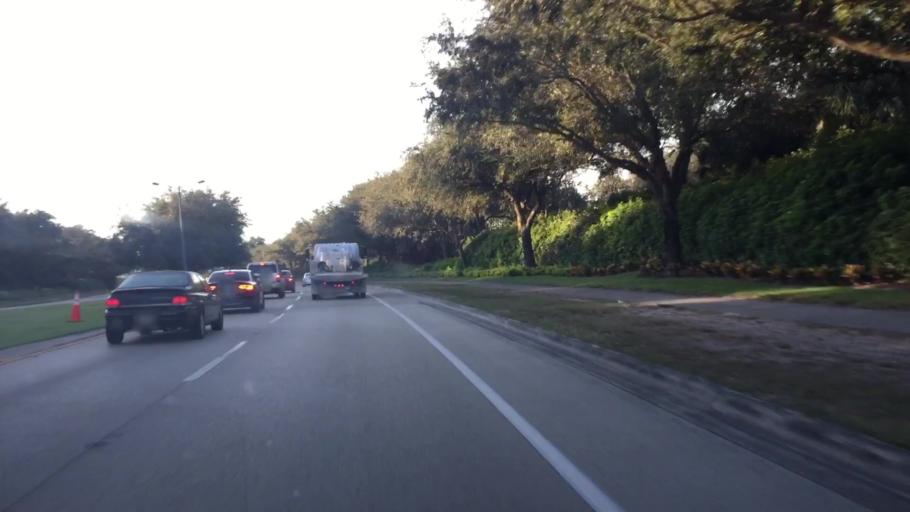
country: US
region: Florida
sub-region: Lee County
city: Three Oaks
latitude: 26.4780
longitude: -81.7867
